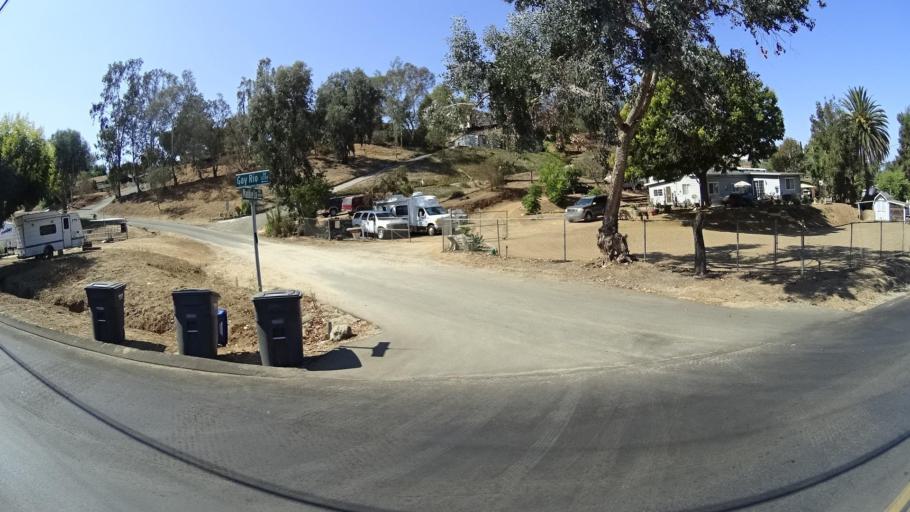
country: US
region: California
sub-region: San Diego County
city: Winter Gardens
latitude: 32.8351
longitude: -116.9269
